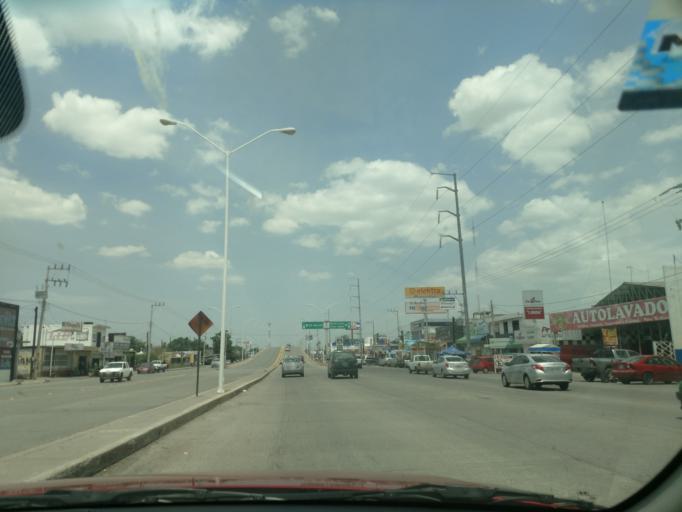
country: MX
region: San Luis Potosi
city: Rio Verde
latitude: 21.9235
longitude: -99.9977
